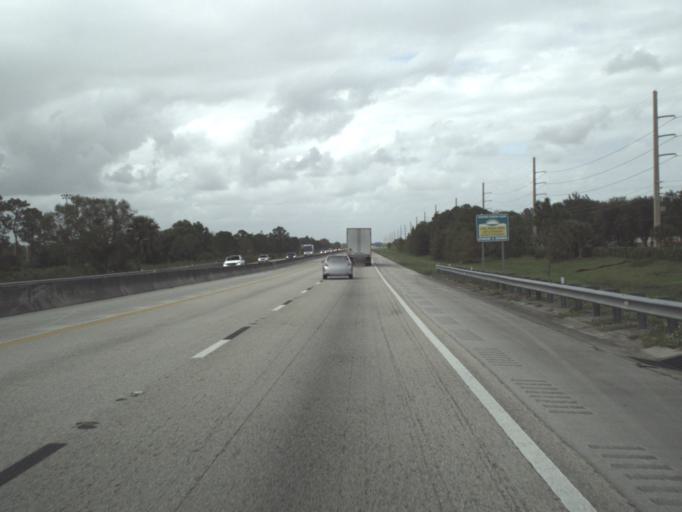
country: US
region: Florida
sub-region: Martin County
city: Palm City
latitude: 27.1756
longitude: -80.3142
